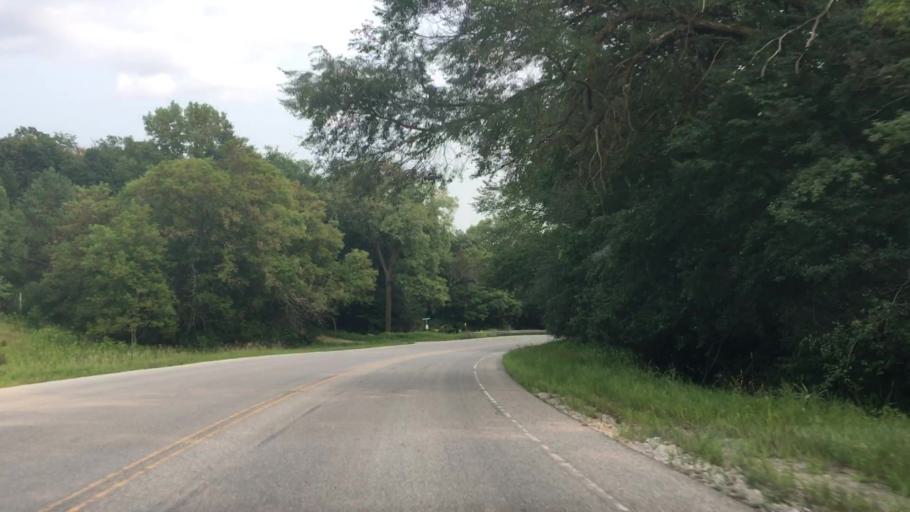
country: US
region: Minnesota
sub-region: Fillmore County
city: Preston
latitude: 43.7265
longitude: -91.9811
